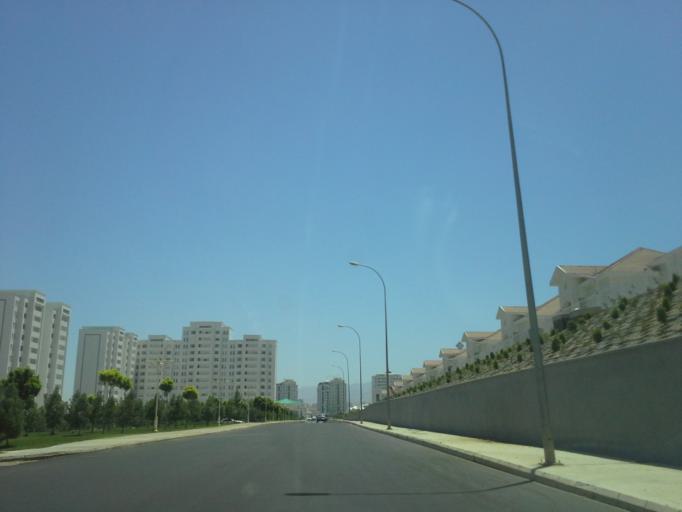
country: TM
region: Ahal
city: Ashgabat
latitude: 37.9340
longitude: 58.3642
